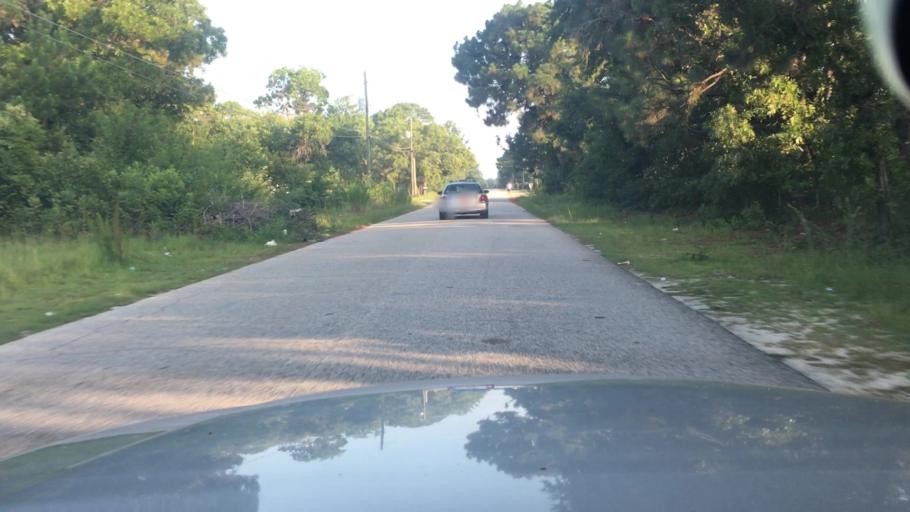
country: US
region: North Carolina
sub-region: Cumberland County
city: Spring Lake
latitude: 35.1109
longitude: -78.9353
